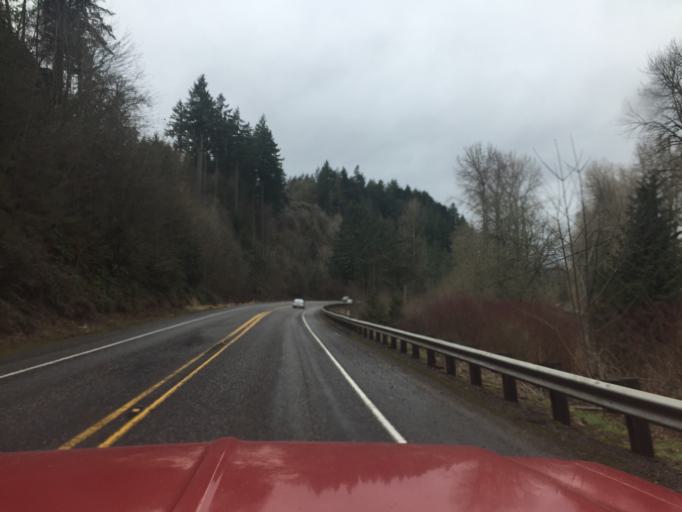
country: US
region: Washington
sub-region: Cowlitz County
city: Kalama
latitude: 46.0226
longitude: -122.8801
